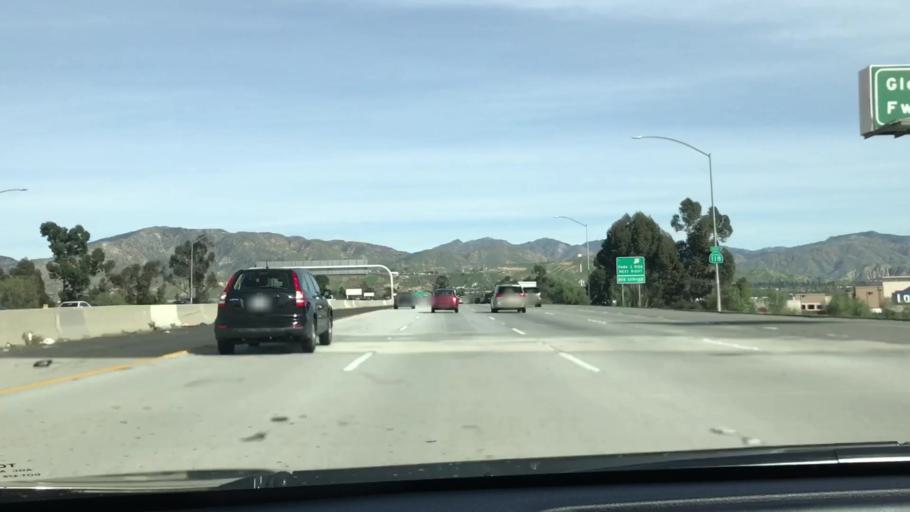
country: US
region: California
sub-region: Los Angeles County
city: San Fernando
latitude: 34.2727
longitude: -118.4284
